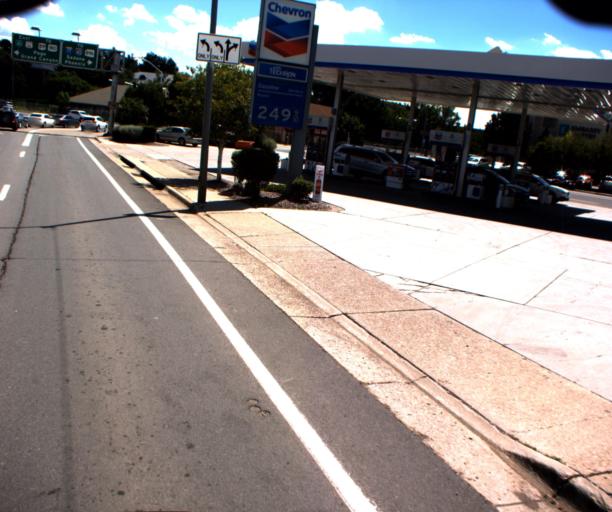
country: US
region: Arizona
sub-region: Coconino County
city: Flagstaff
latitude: 35.1928
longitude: -111.6595
